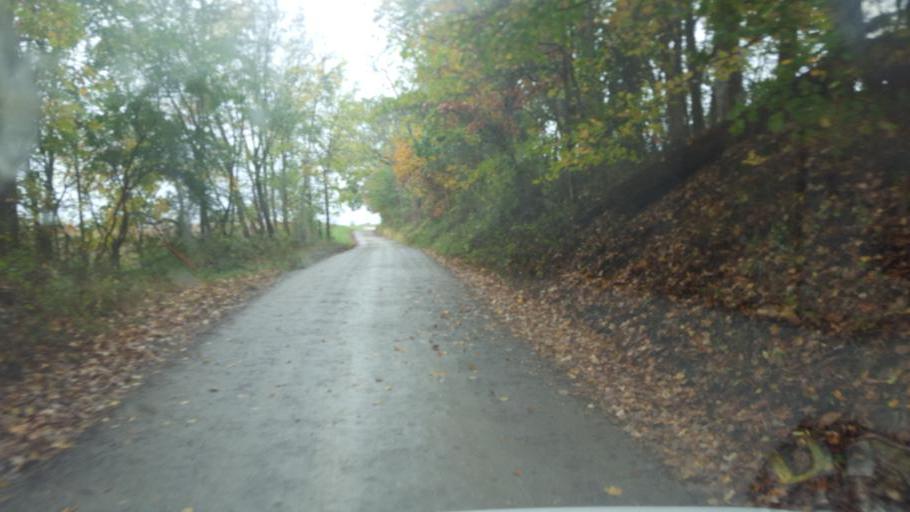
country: US
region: Ohio
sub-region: Holmes County
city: Millersburg
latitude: 40.5875
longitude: -81.9935
